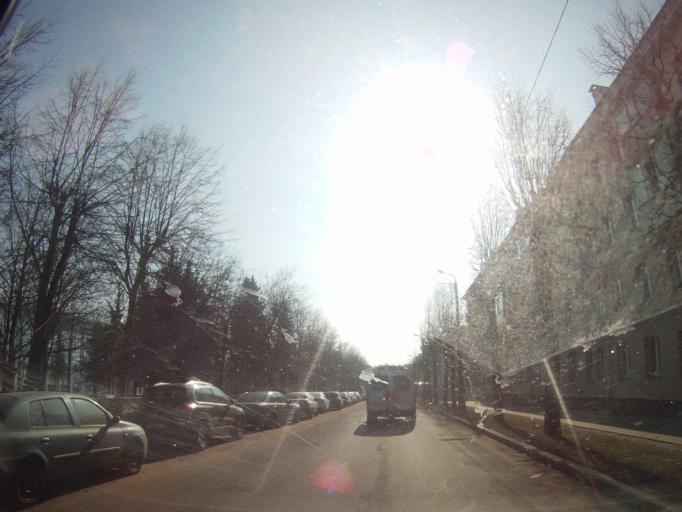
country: BY
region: Minsk
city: Minsk
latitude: 53.9267
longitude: 27.6125
